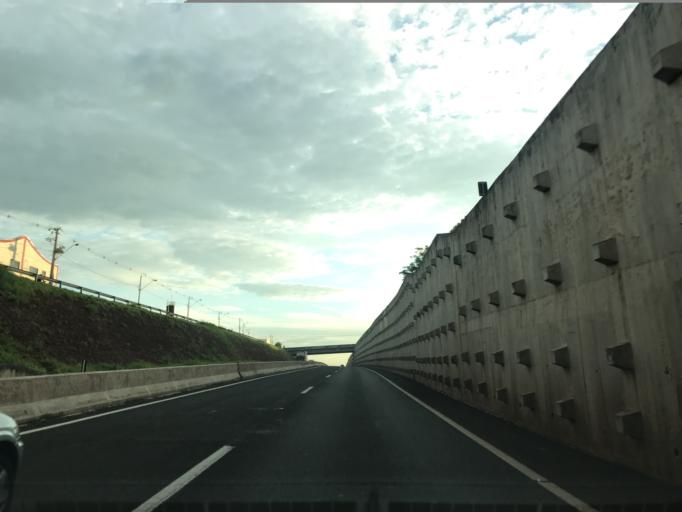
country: BR
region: Parana
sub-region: Maringa
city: Maringa
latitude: -23.3779
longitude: -51.9439
